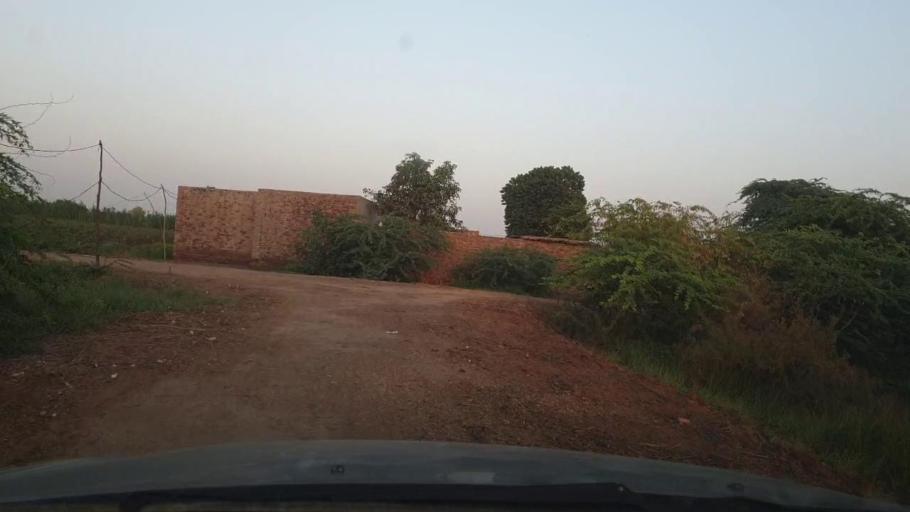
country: PK
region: Sindh
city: Tando Ghulam Ali
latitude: 25.1202
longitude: 68.9863
